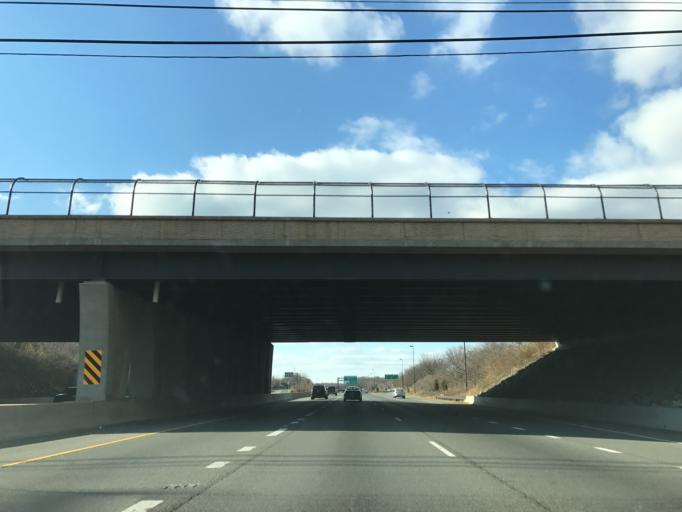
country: US
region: Maryland
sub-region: Montgomery County
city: North Bethesda
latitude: 39.0306
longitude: -77.1257
